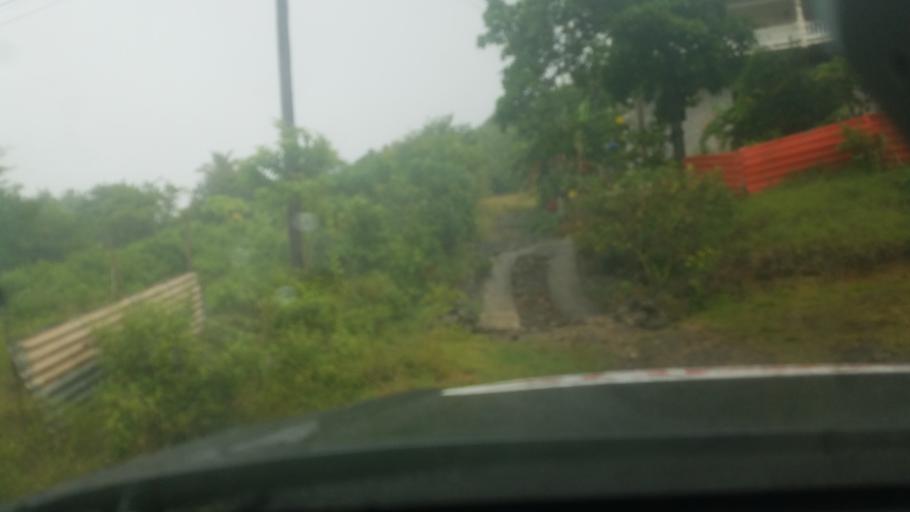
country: LC
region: Gros-Islet
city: Gros Islet
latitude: 14.0465
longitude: -60.9394
